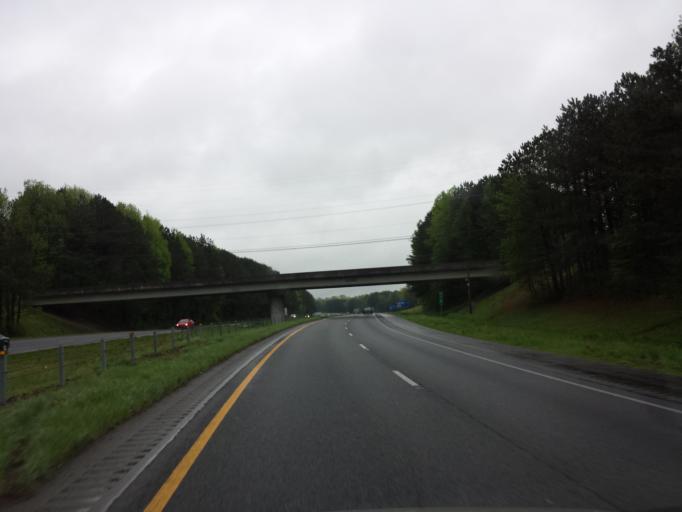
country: US
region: Georgia
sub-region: Cherokee County
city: Holly Springs
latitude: 34.1966
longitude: -84.5021
